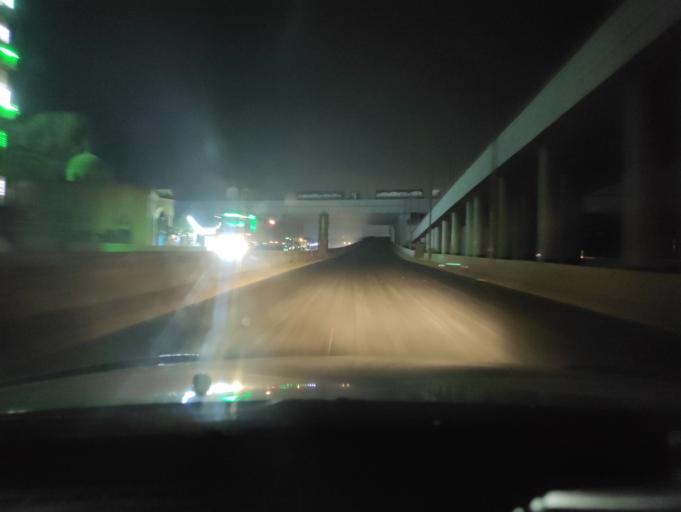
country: EG
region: Muhafazat al Qalyubiyah
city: Banha
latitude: 30.4978
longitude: 31.1664
